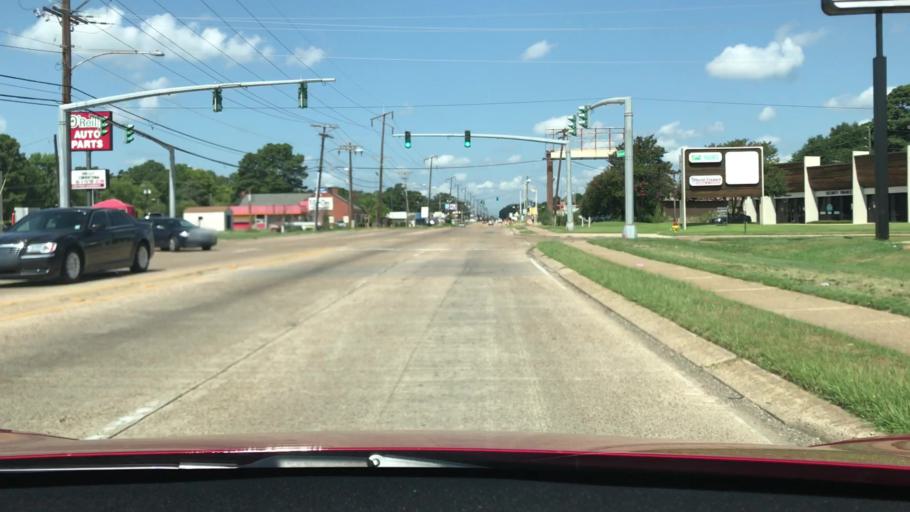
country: US
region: Louisiana
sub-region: Caddo Parish
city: Shreveport
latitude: 32.4420
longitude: -93.7836
